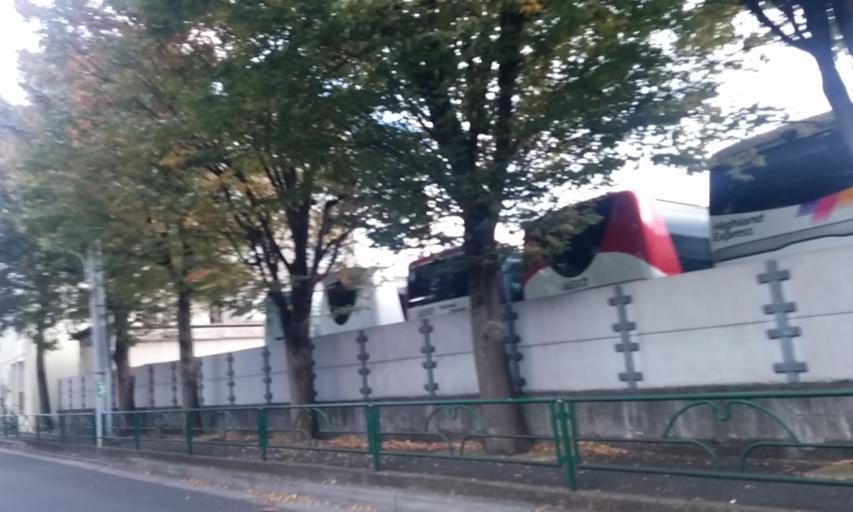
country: JP
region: Tokyo
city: Tokyo
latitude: 35.6774
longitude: 139.6402
